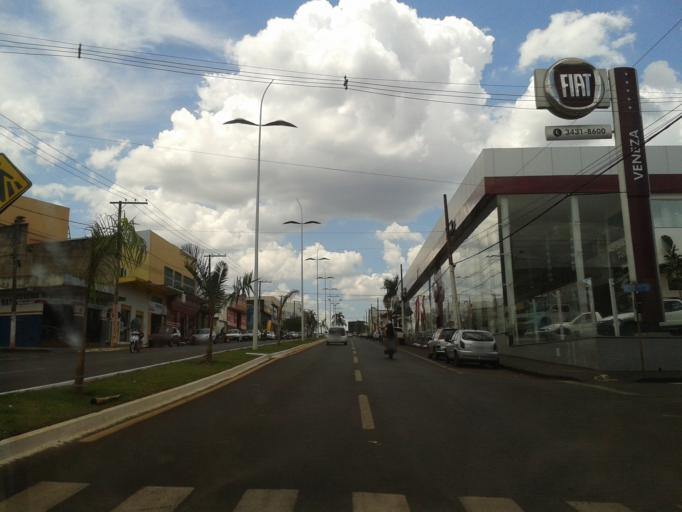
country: BR
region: Goias
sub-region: Itumbiara
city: Itumbiara
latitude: -18.4083
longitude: -49.2120
